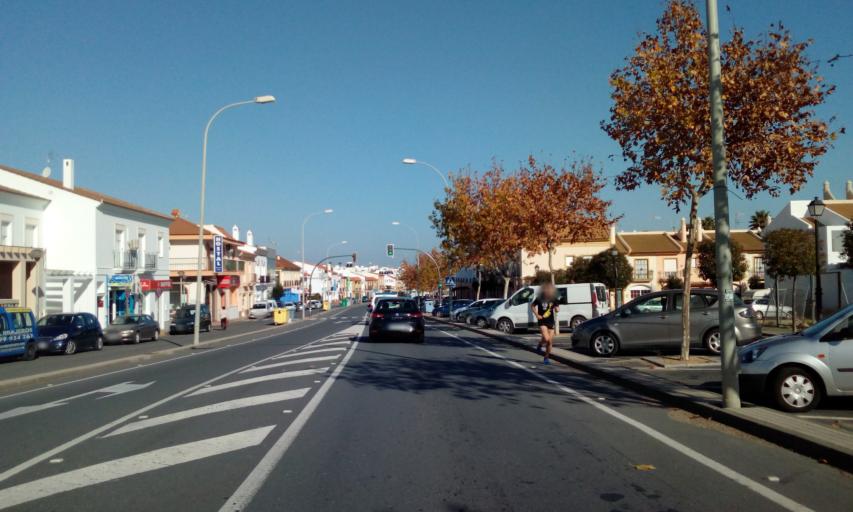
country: ES
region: Andalusia
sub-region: Provincia de Huelva
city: Lepe
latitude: 37.2464
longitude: -7.2034
